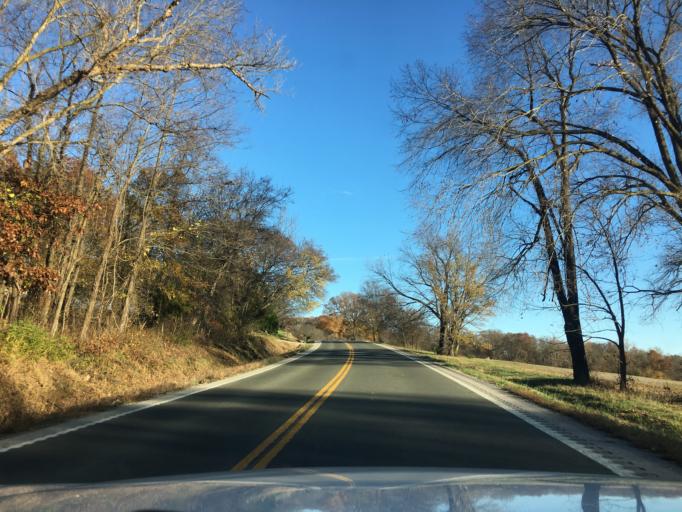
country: US
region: Missouri
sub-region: Franklin County
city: New Haven
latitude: 38.5988
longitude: -91.2534
